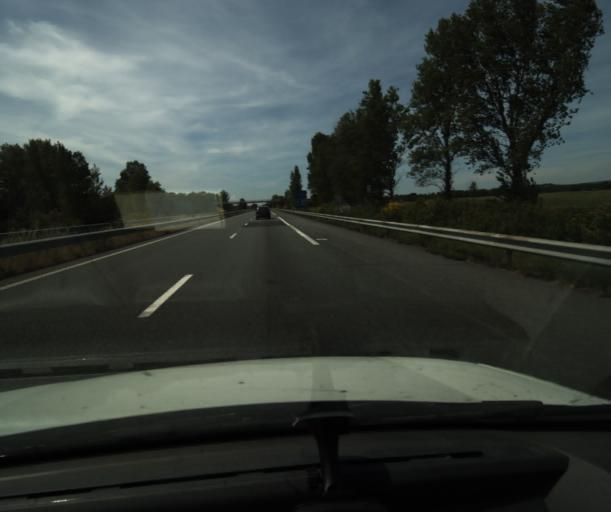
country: FR
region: Languedoc-Roussillon
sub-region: Departement de l'Aude
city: Saint-Martin-Lalande
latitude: 43.2718
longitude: 2.0018
